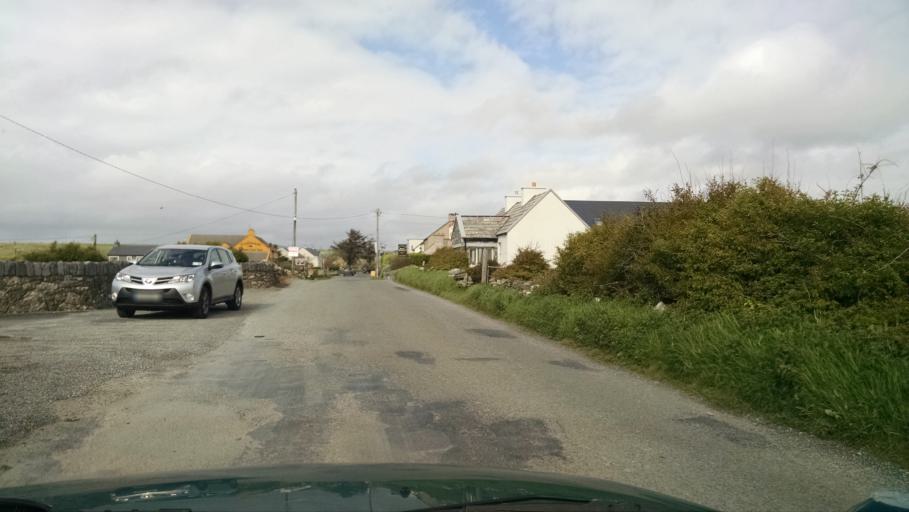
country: IE
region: Connaught
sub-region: County Galway
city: Bearna
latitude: 53.0153
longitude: -9.3786
